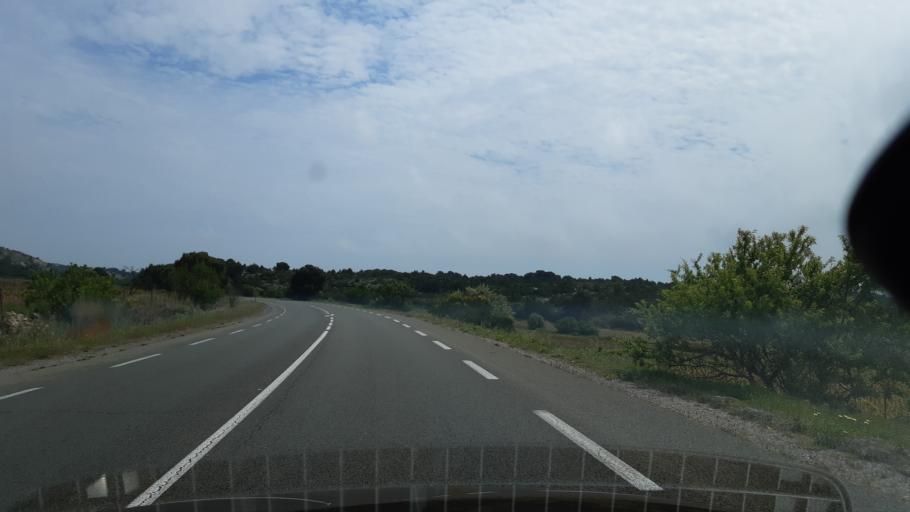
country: FR
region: Languedoc-Roussillon
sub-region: Departement de l'Aude
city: Gruissan
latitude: 43.1252
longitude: 3.0635
